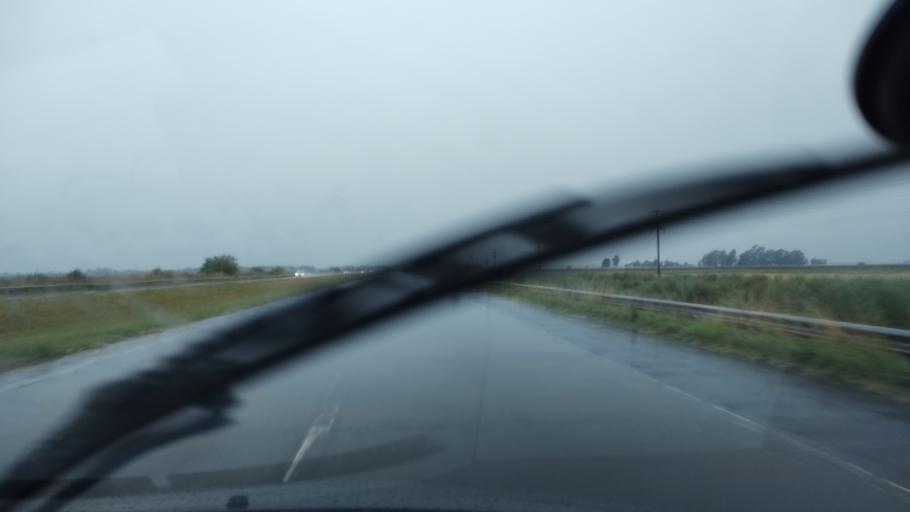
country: AR
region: Buenos Aires
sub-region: Partido de San Vicente
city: San Vicente
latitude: -35.0642
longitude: -58.4747
